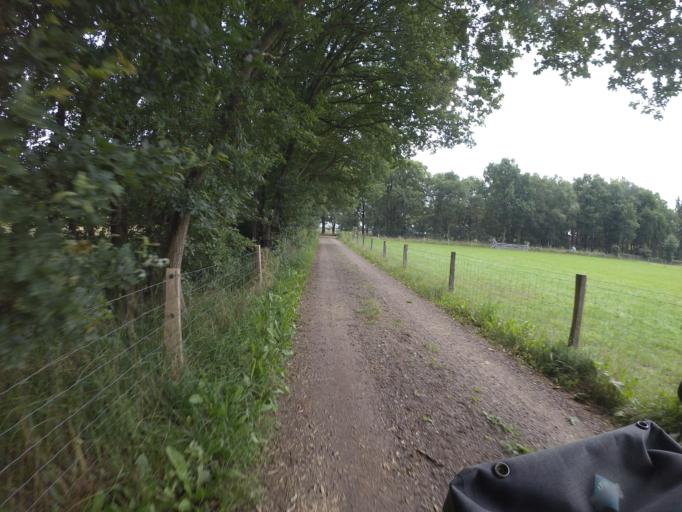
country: NL
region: Gelderland
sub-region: Gemeente Barneveld
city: Garderen
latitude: 52.2667
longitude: 5.7166
